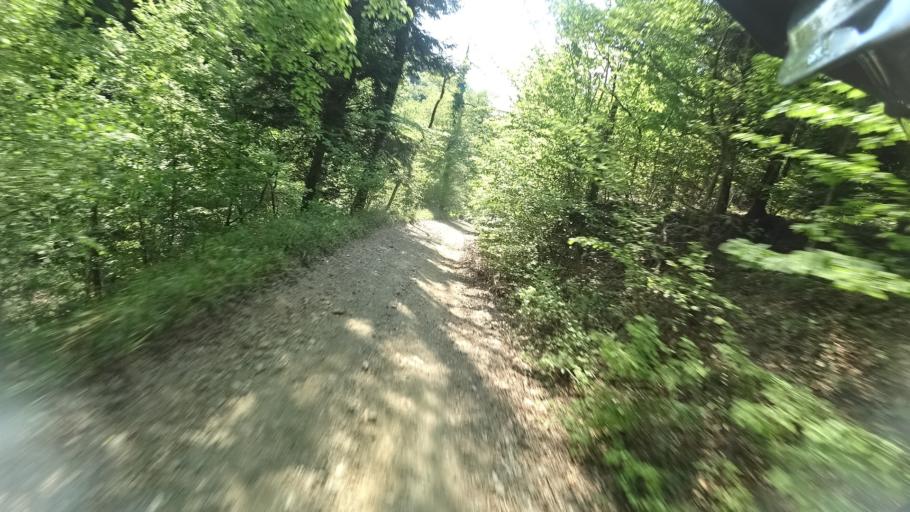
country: HR
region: Grad Zagreb
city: Kasina
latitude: 45.9491
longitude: 15.9900
